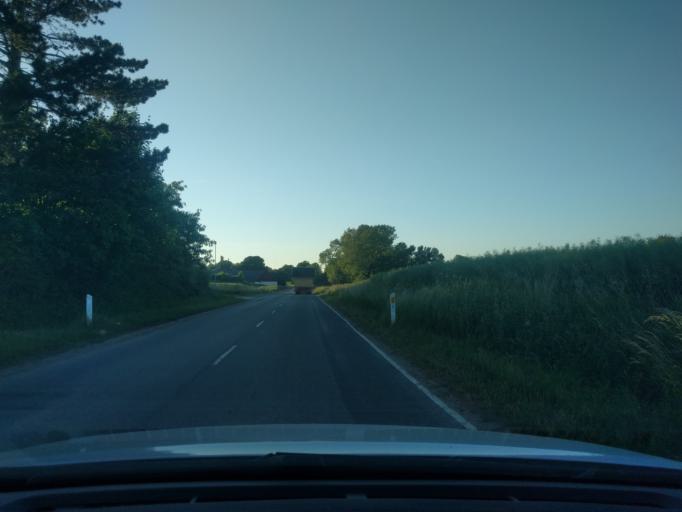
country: DK
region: South Denmark
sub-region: Kerteminde Kommune
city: Kerteminde
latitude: 55.5939
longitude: 10.6280
